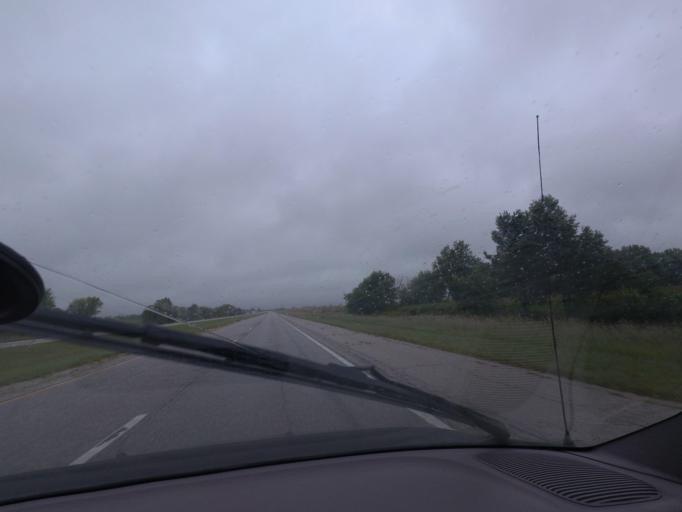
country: US
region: Illinois
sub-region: Pike County
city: Pittsfield
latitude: 39.6725
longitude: -90.8495
